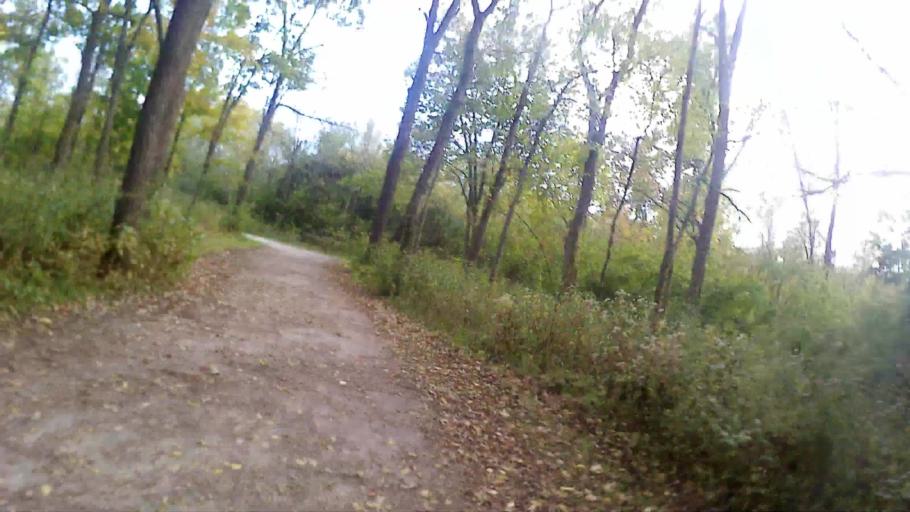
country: US
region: Illinois
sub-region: DuPage County
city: Warrenville
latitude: 41.8237
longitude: -88.1393
